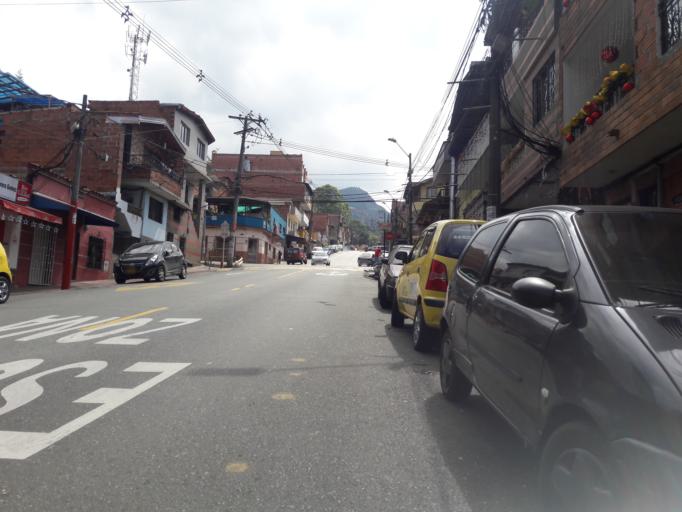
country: CO
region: Antioquia
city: Medellin
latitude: 6.2578
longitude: -75.5510
